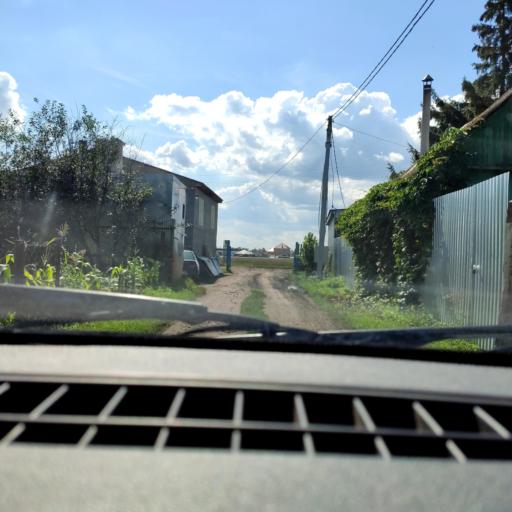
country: RU
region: Bashkortostan
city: Ufa
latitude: 54.6360
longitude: 55.9194
